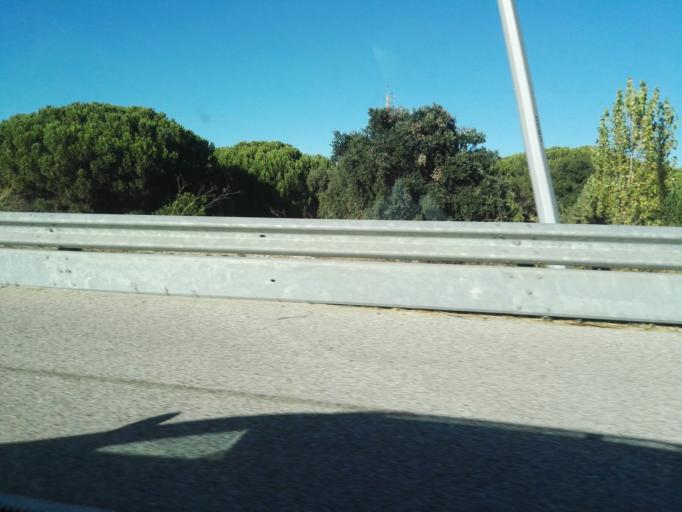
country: PT
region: Santarem
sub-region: Benavente
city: Benavente
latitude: 38.9642
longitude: -8.8369
